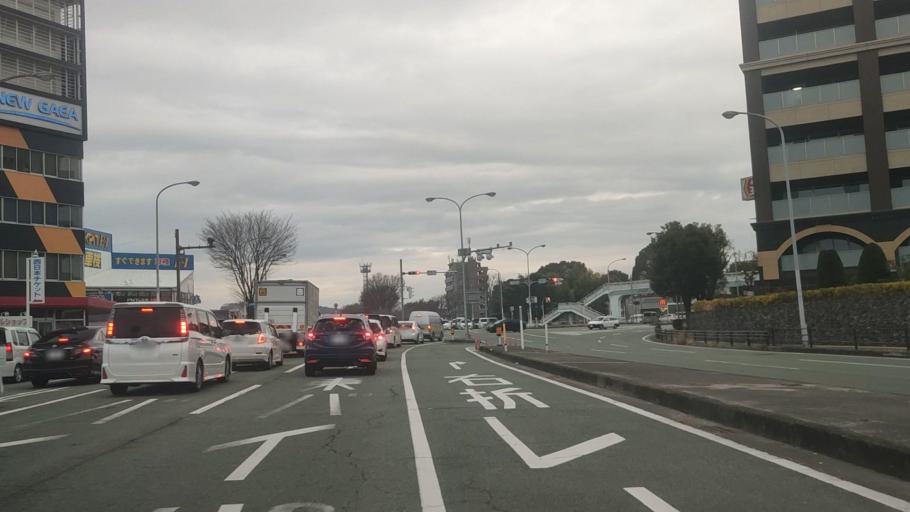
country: JP
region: Kumamoto
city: Kumamoto
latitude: 32.8154
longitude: 130.7505
